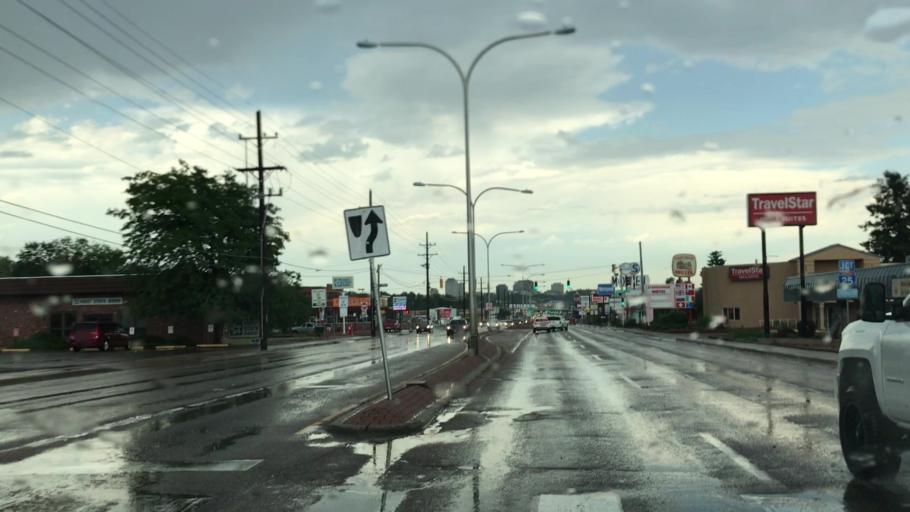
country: US
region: Colorado
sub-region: El Paso County
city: Colorado Springs
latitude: 38.8087
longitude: -104.8223
